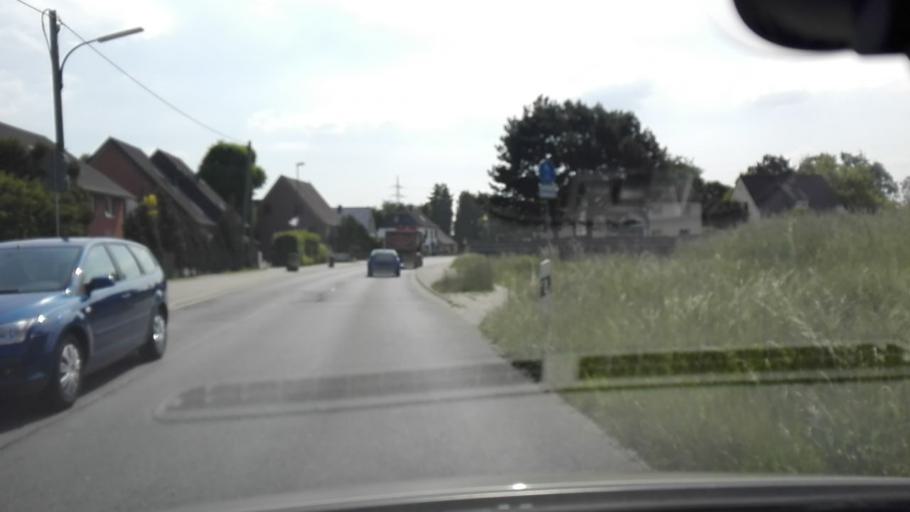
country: DE
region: North Rhine-Westphalia
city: Lanstrop
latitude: 51.6076
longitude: 7.5795
